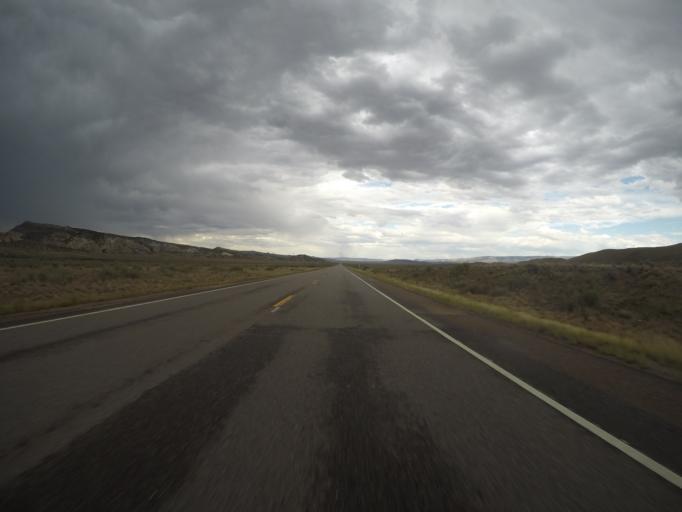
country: US
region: Colorado
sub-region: Rio Blanco County
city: Rangely
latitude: 40.2509
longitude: -108.7874
